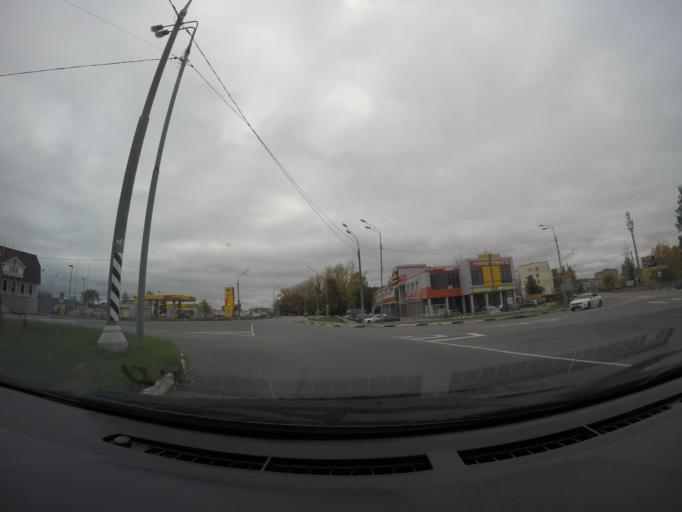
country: RU
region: Moskovskaya
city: Ruza
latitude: 55.7101
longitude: 36.2038
